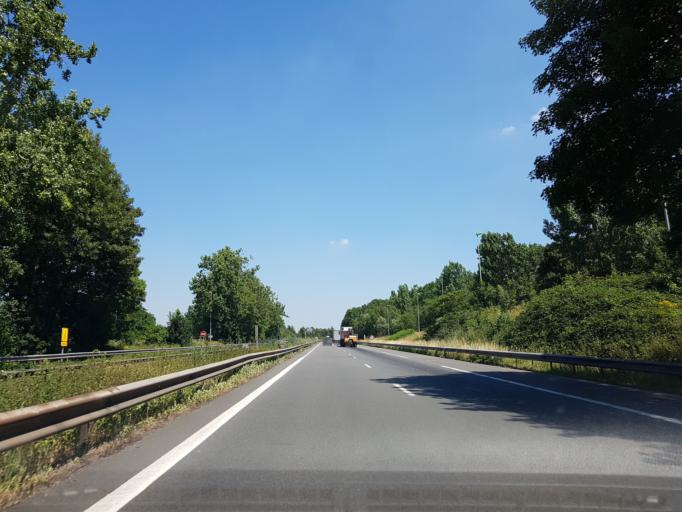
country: FR
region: Nord-Pas-de-Calais
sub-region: Departement du Nord
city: Lieu-Saint-Amand
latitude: 50.2675
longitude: 3.3329
